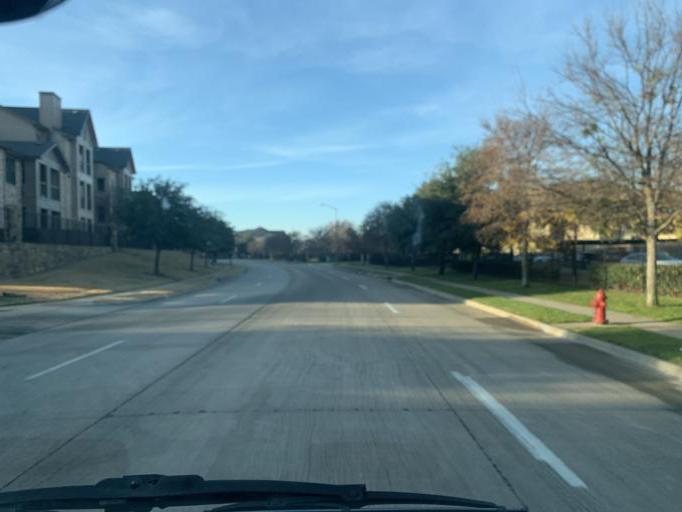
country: US
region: Texas
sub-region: Tarrant County
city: Euless
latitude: 32.7924
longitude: -97.0615
